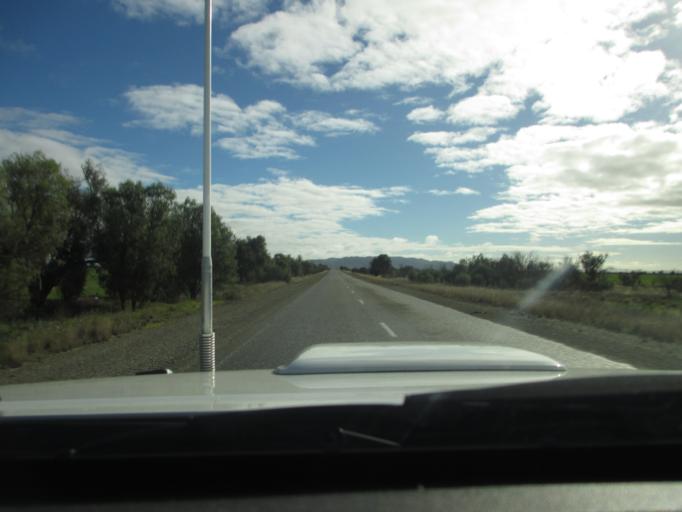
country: AU
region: South Australia
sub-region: Peterborough
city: Peterborough
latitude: -32.6779
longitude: 138.6082
